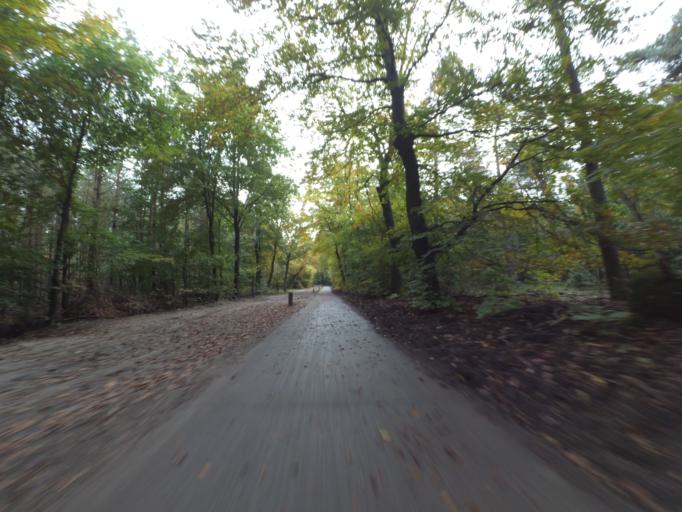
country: NL
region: Gelderland
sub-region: Gemeente Nunspeet
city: Nunspeet
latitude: 52.3238
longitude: 5.7460
